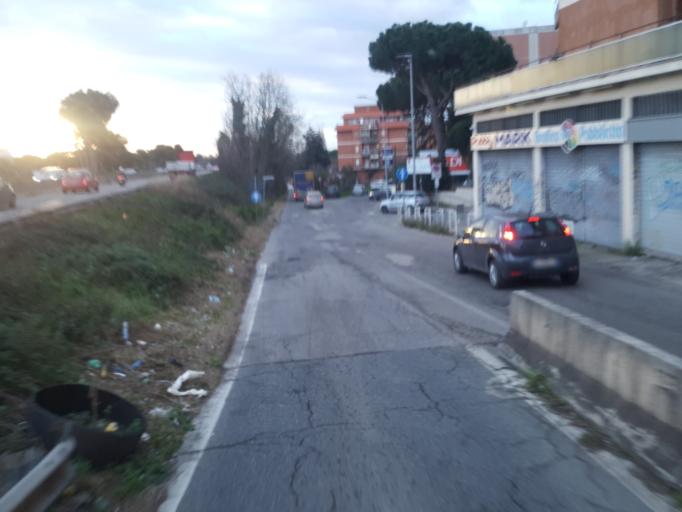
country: IT
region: Latium
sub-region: Citta metropolitana di Roma Capitale
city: Area Produttiva
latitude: 41.6750
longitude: 12.5014
